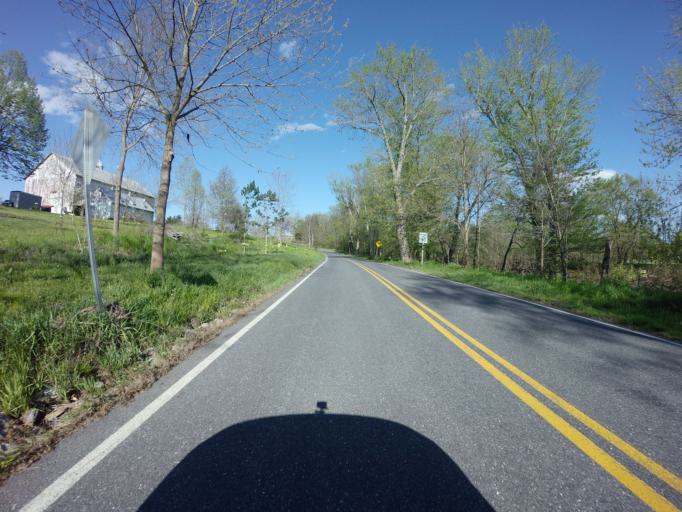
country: US
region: Maryland
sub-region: Frederick County
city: Emmitsburg
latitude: 39.6311
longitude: -77.2876
